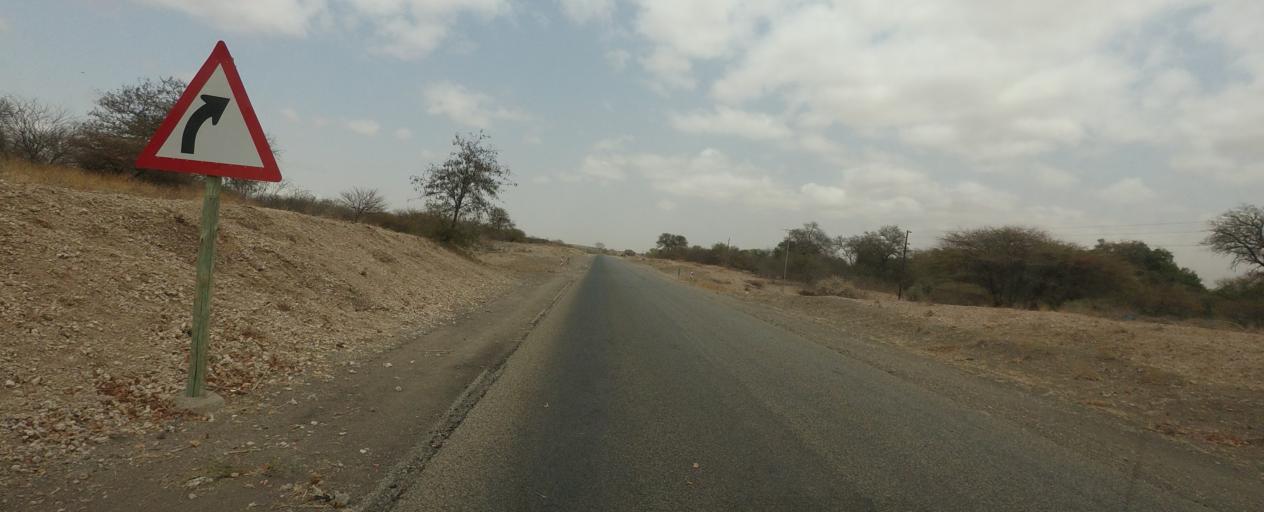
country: ZA
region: Limpopo
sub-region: Vhembe District Municipality
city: Mutale
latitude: -22.4578
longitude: 30.4947
